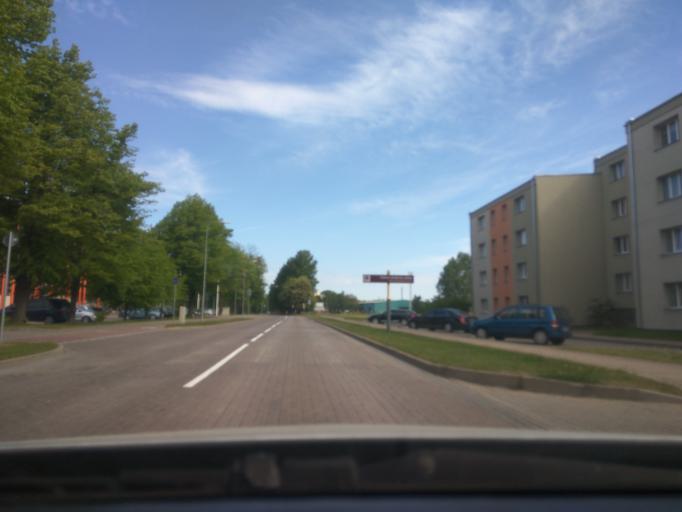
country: LV
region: Ventspils
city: Ventspils
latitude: 57.3939
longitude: 21.5732
